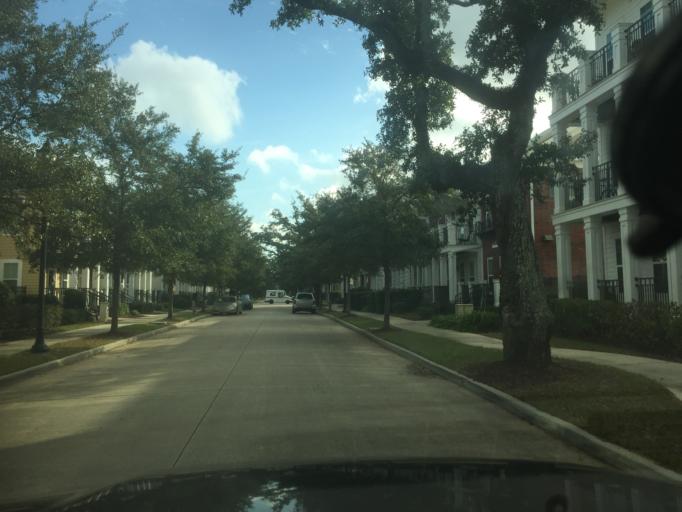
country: US
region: Louisiana
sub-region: Orleans Parish
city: New Orleans
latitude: 29.9978
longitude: -90.0761
